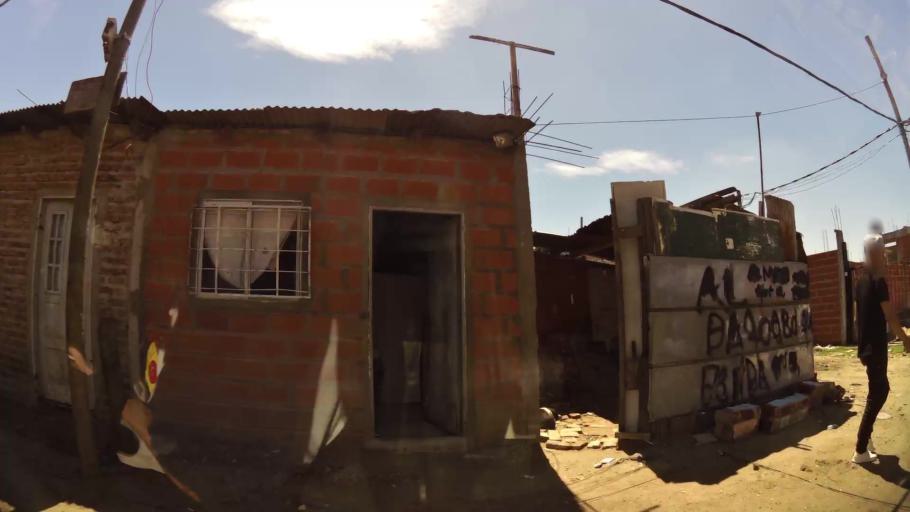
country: AR
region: Buenos Aires
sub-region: Partido de Quilmes
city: Quilmes
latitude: -34.7294
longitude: -58.3169
